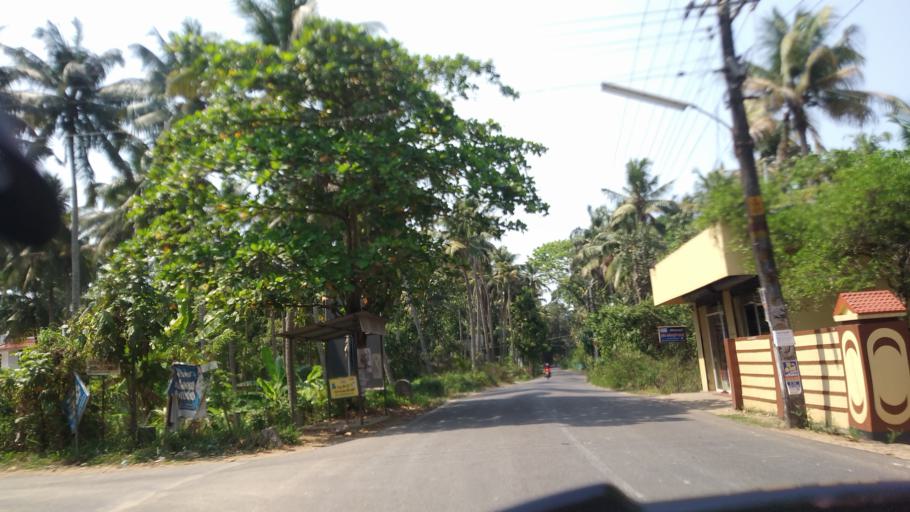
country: IN
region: Kerala
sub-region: Thrissur District
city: Kodungallur
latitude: 10.2697
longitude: 76.1410
